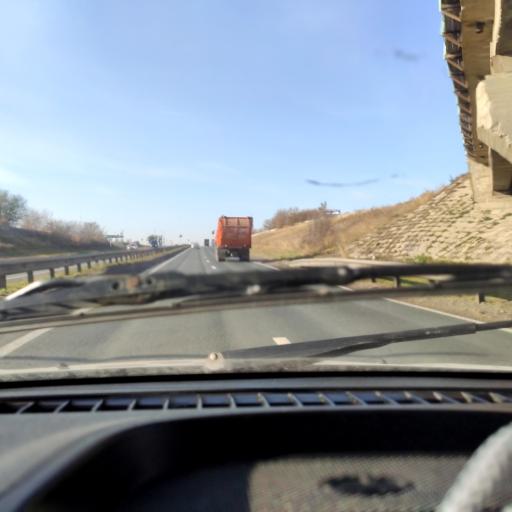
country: RU
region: Samara
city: Tol'yatti
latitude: 53.5690
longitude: 49.4822
